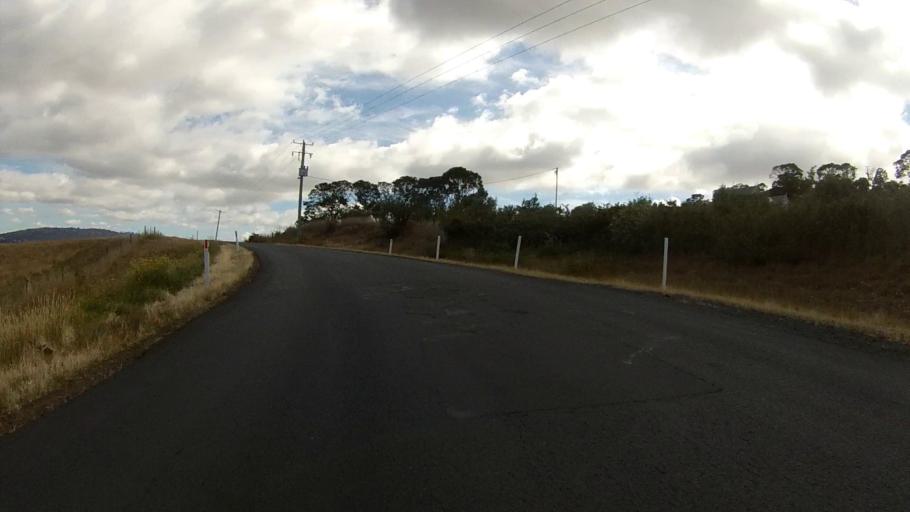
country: AU
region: Tasmania
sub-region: Brighton
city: Old Beach
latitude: -42.7586
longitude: 147.3044
